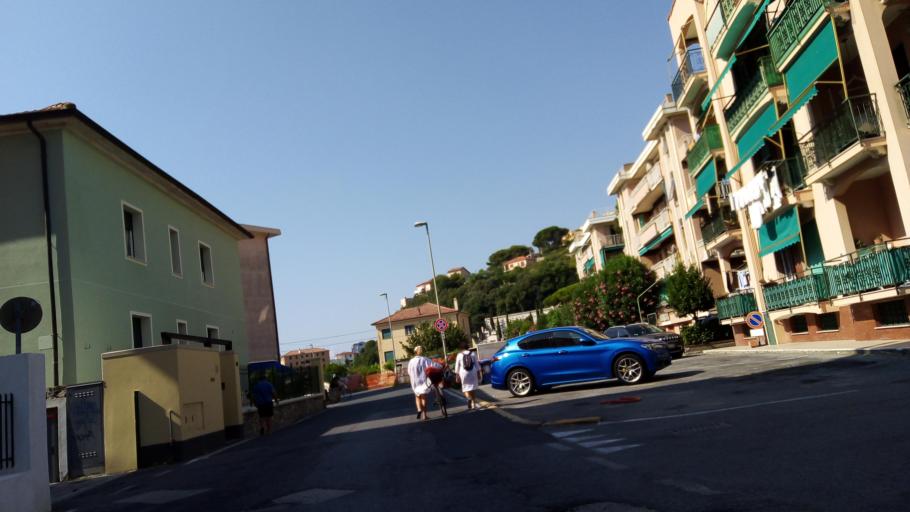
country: IT
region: Liguria
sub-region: Provincia di Savona
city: Pietra Ligure
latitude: 44.1542
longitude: 8.2866
